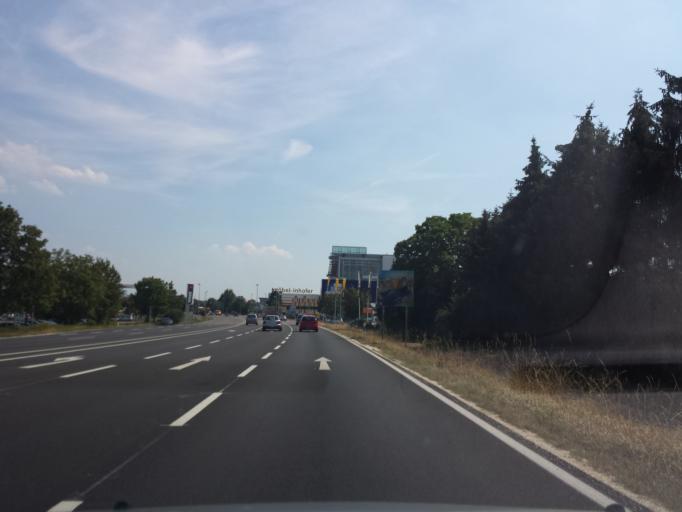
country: DE
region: Bavaria
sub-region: Swabia
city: Senden
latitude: 48.3322
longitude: 10.0360
